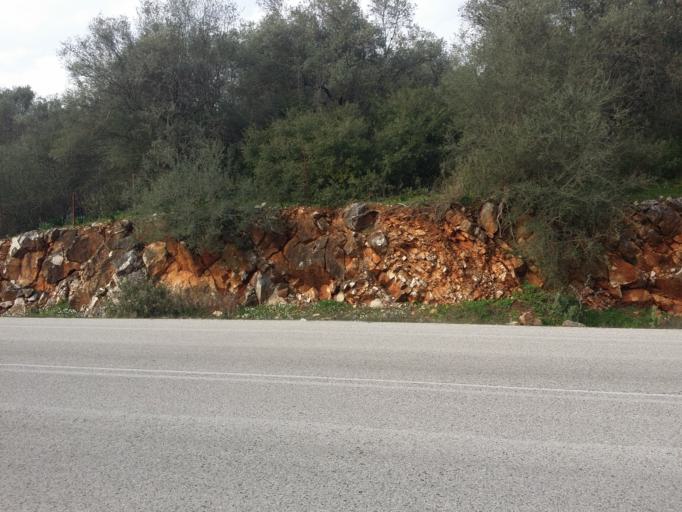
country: GR
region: West Greece
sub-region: Nomos Aitolias kai Akarnanias
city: Stanos
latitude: 38.7695
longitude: 21.1678
